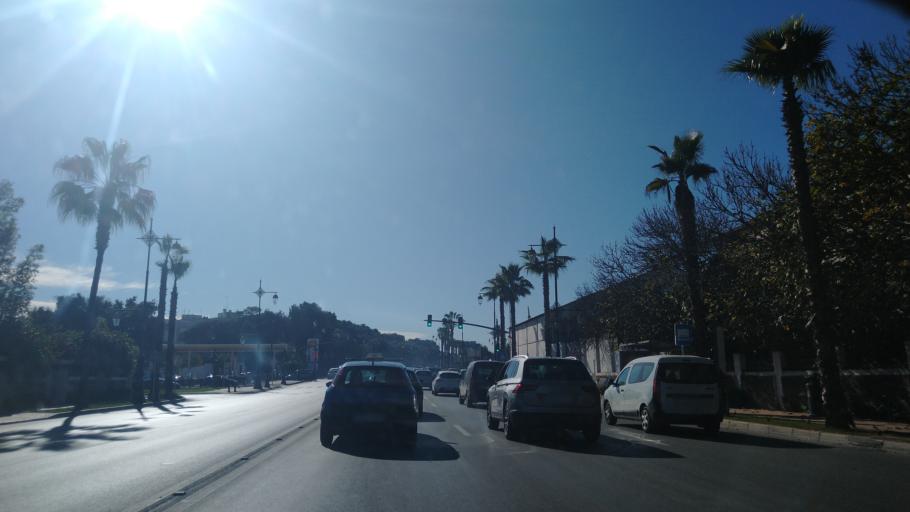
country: MA
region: Rabat-Sale-Zemmour-Zaer
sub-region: Rabat
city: Rabat
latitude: 33.9946
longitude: -6.8274
